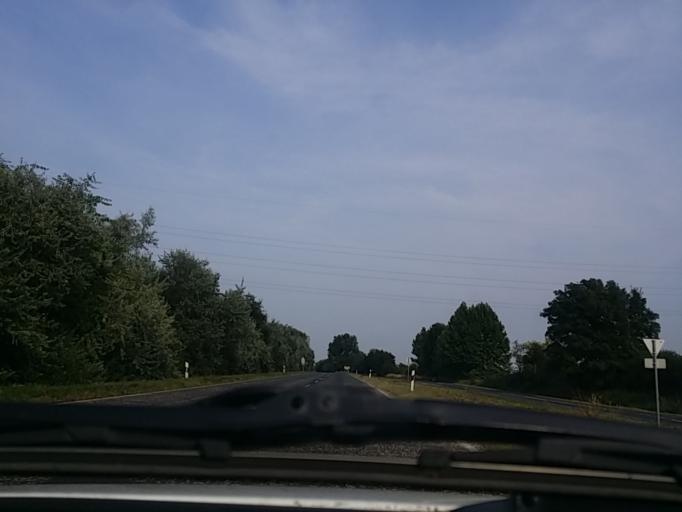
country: HU
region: Fejer
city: Bicske
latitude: 47.4947
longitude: 18.6909
